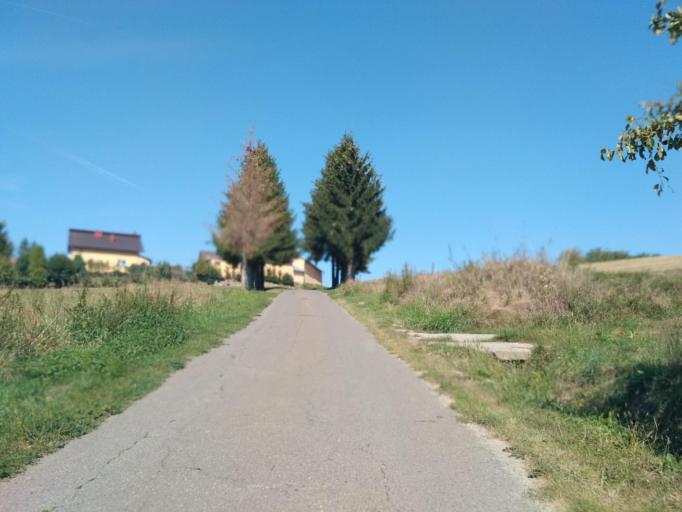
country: PL
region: Subcarpathian Voivodeship
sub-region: Powiat brzozowski
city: Grabownica Starzenska
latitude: 49.6545
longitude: 22.0853
